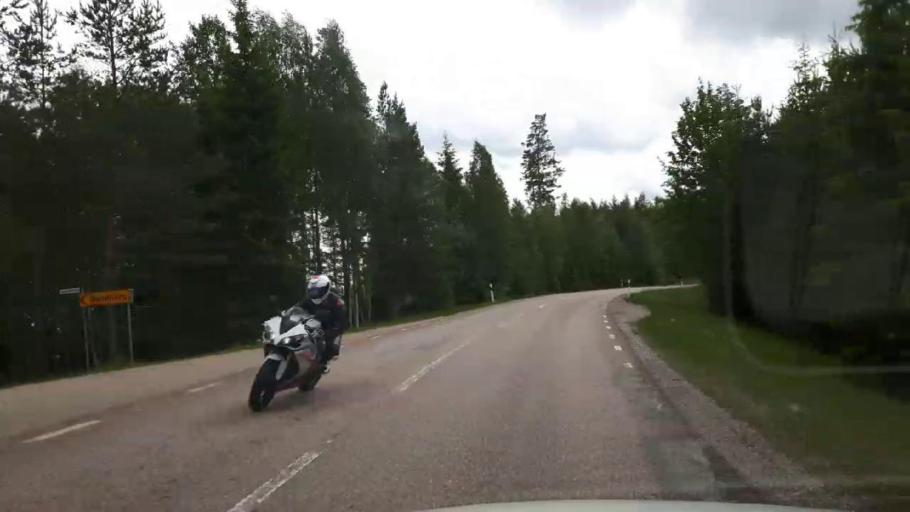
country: SE
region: Vaestmanland
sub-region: Fagersta Kommun
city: Fagersta
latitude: 59.9228
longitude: 15.8311
